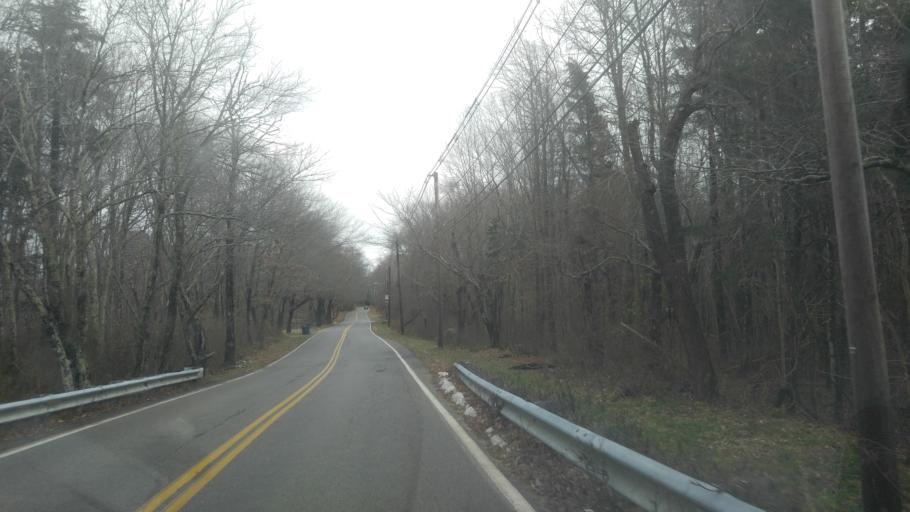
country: US
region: Rhode Island
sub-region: Kent County
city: West Warwick
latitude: 41.6429
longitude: -71.5274
